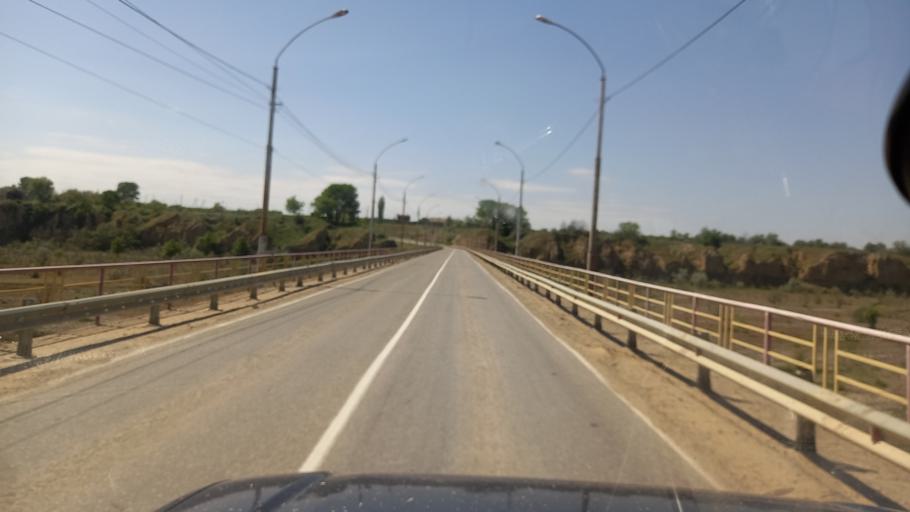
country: RU
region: Dagestan
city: Novaya Maka
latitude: 41.7370
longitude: 48.4475
